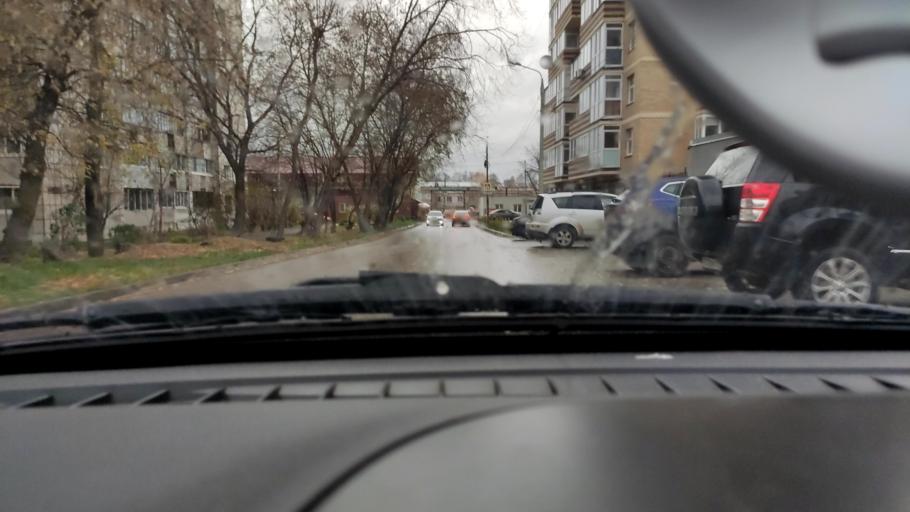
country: RU
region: Perm
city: Perm
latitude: 57.9886
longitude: 56.2142
